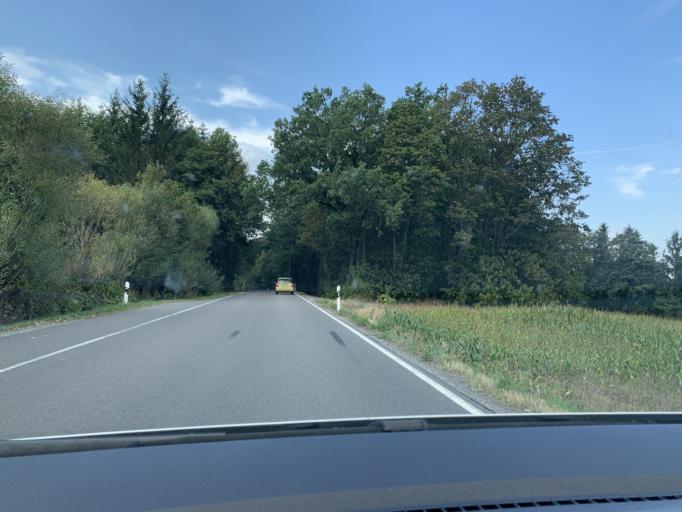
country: DE
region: Saxony
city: Falkenau
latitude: 50.9078
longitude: 13.1082
